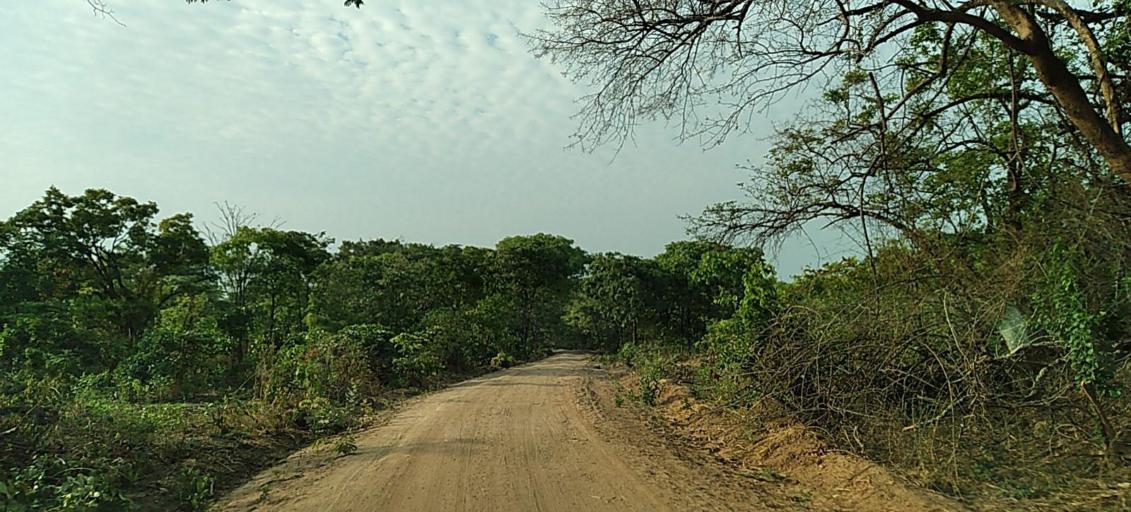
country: ZM
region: Copperbelt
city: Chingola
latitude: -12.8760
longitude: 27.6913
